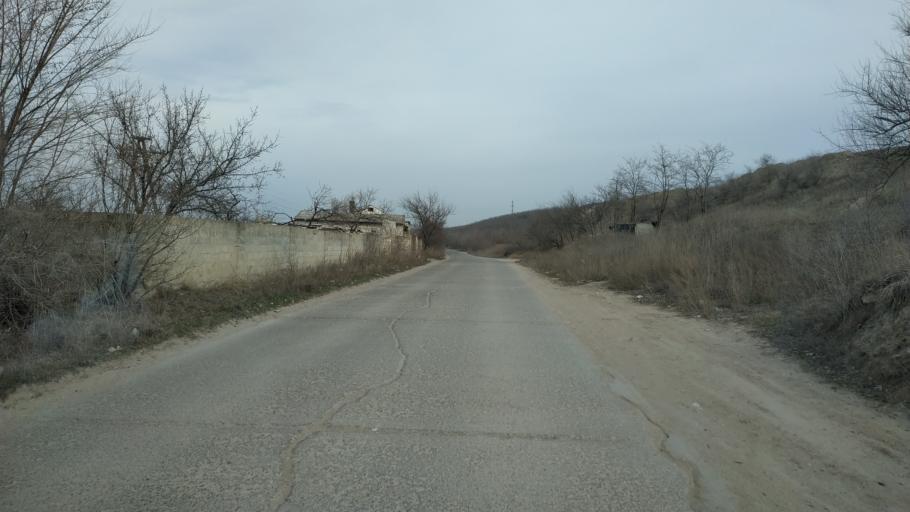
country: MD
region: Chisinau
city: Vatra
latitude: 47.0798
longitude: 28.7416
